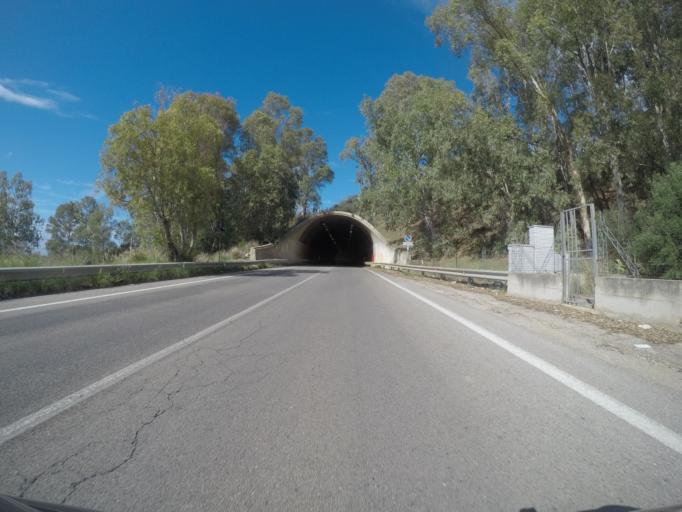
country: IT
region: Sicily
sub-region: Palermo
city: Agliandroni-Paternella
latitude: 38.1231
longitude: 13.0763
